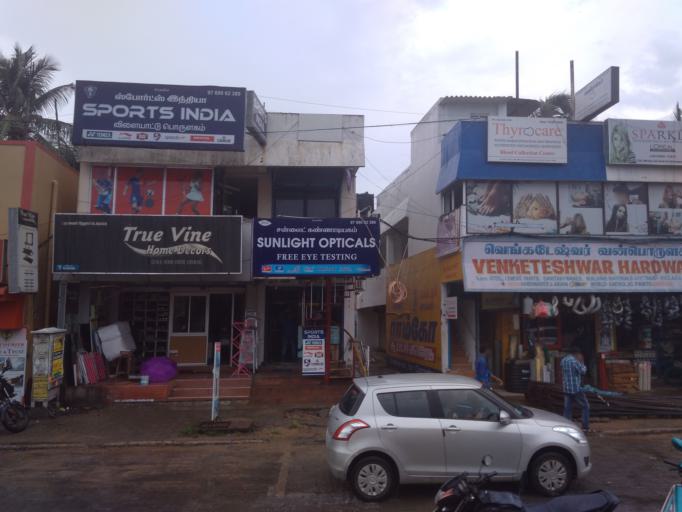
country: IN
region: Tamil Nadu
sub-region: Kancheepuram
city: Perungudi
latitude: 12.9412
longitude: 80.2360
